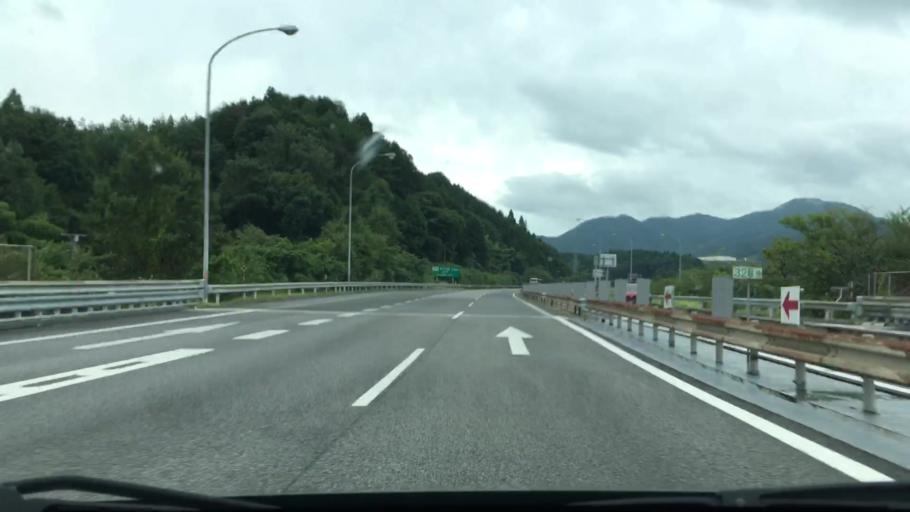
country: JP
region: Hiroshima
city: Hiroshima-shi
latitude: 34.6716
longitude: 132.5423
